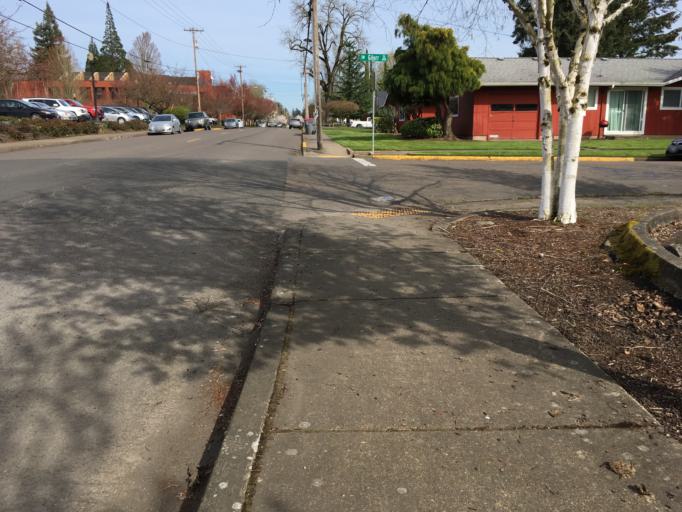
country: US
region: Oregon
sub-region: Yamhill County
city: McMinnville
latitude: 45.2002
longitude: -123.2036
